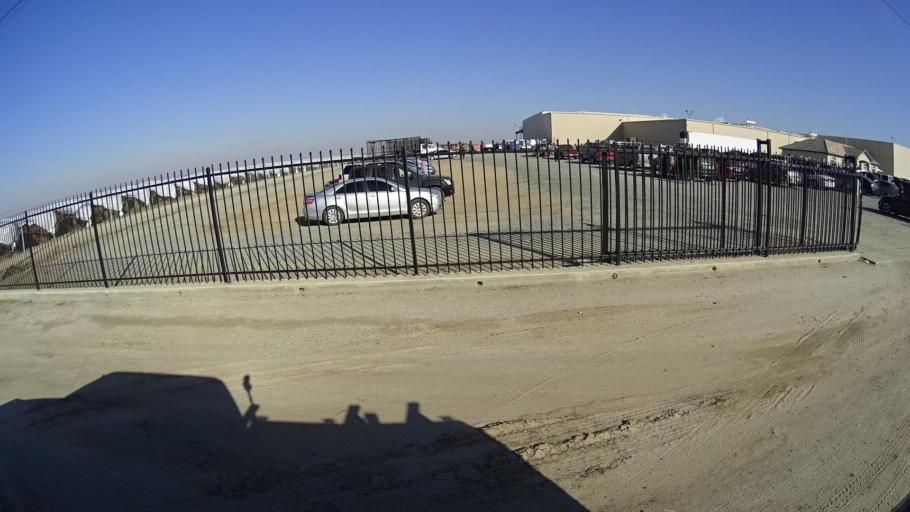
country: US
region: California
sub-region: Tulare County
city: Richgrove
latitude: 35.7471
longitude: -119.1449
